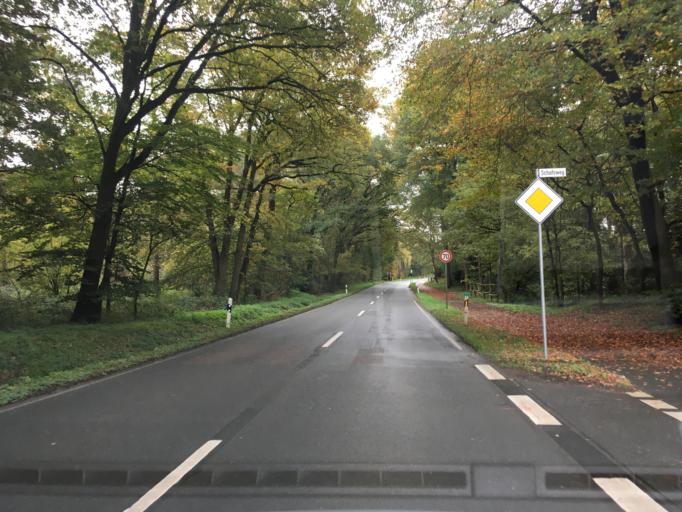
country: DE
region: North Rhine-Westphalia
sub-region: Regierungsbezirk Munster
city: Heiden
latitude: 51.8243
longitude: 6.9558
